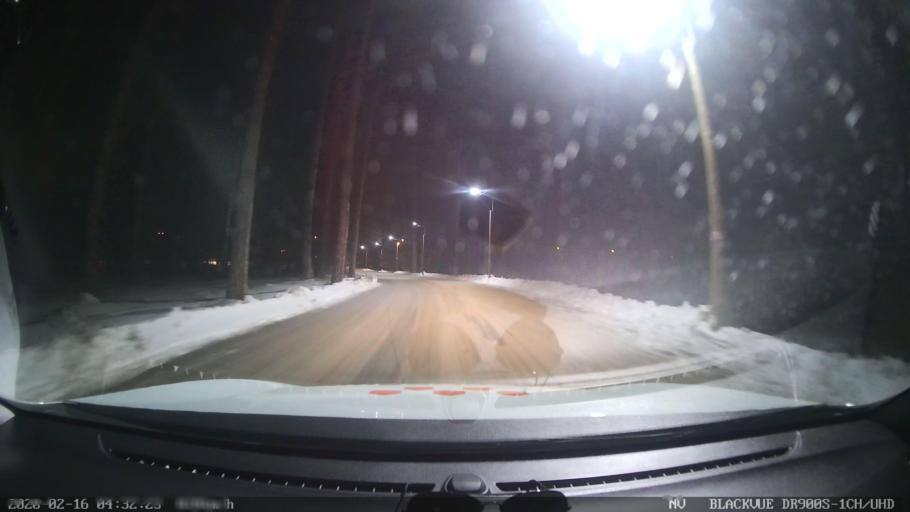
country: RU
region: Tatarstan
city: Staroye Arakchino
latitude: 55.8359
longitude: 48.9657
